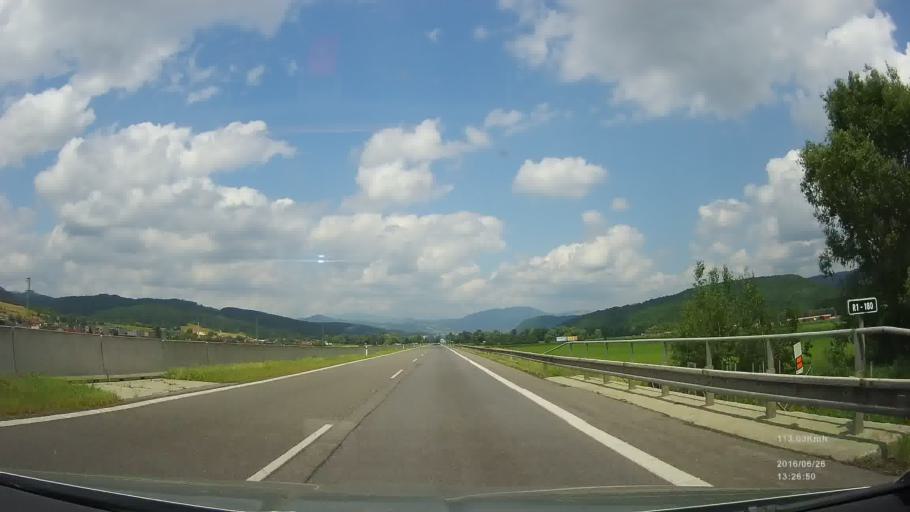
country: SK
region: Banskobystricky
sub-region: Okres Banska Bystrica
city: Banska Bystrica
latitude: 48.6728
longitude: 19.1327
